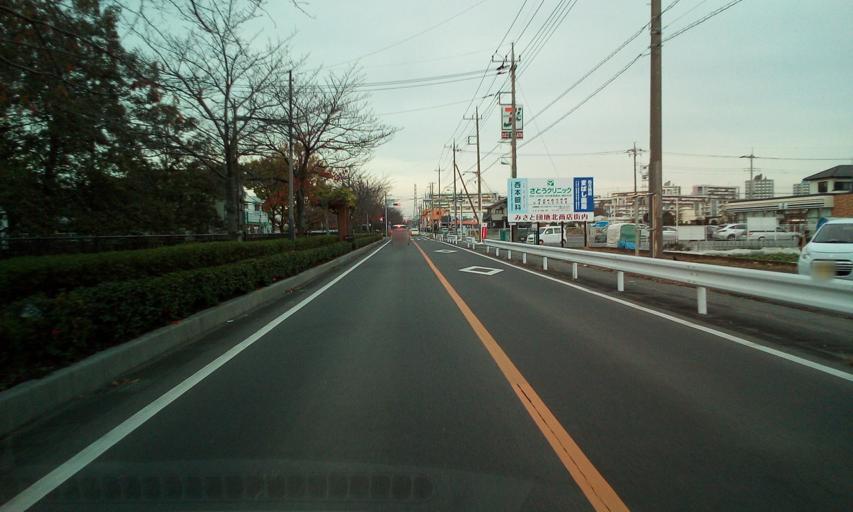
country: JP
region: Saitama
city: Yashio-shi
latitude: 35.8520
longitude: 139.8535
